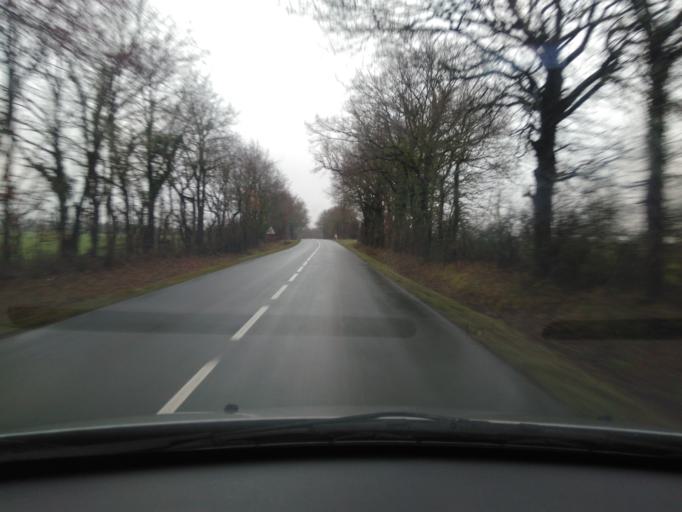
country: FR
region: Pays de la Loire
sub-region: Departement de la Vendee
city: La Chaize-le-Vicomte
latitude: 46.6885
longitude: -1.3043
